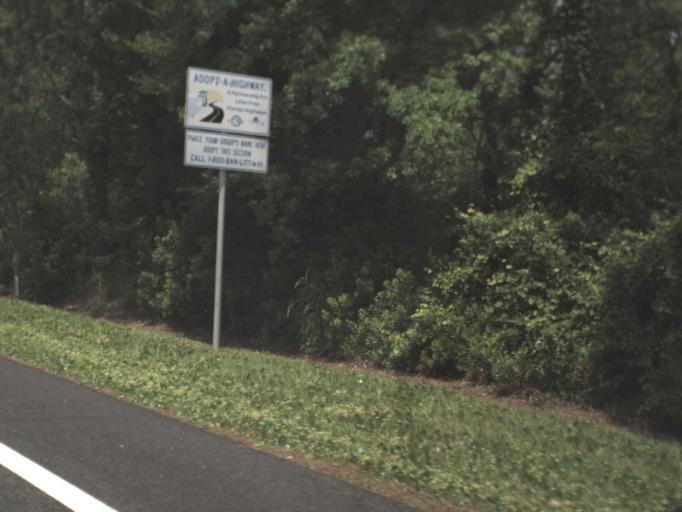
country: US
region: Florida
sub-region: Duval County
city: Baldwin
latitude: 30.2590
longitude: -81.8672
